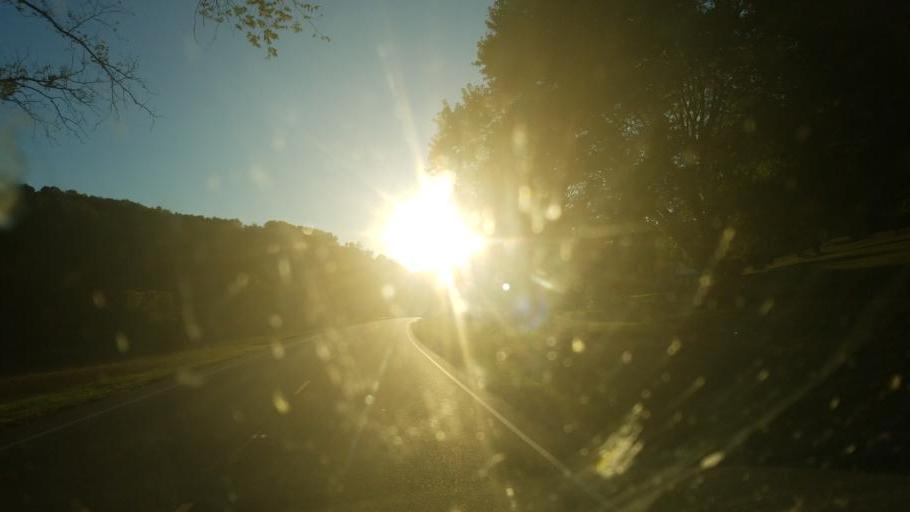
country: US
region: Ohio
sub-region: Knox County
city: Oak Hill
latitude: 40.3378
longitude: -82.0772
